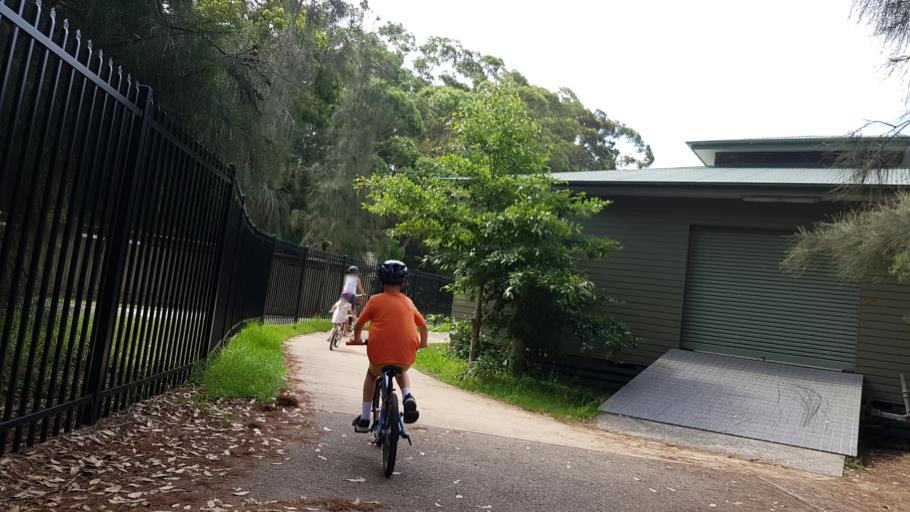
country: AU
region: New South Wales
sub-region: Pittwater
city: North Narrabeen
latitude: -33.7205
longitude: 151.2714
